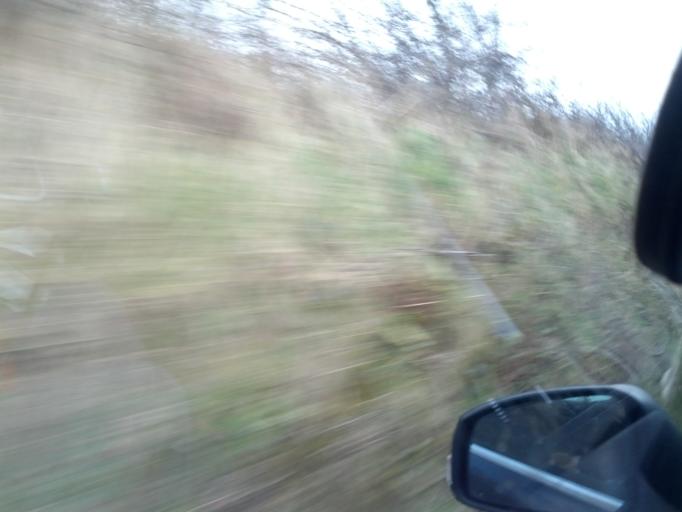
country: IE
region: Connaught
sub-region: County Galway
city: Athenry
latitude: 53.4527
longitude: -8.6672
